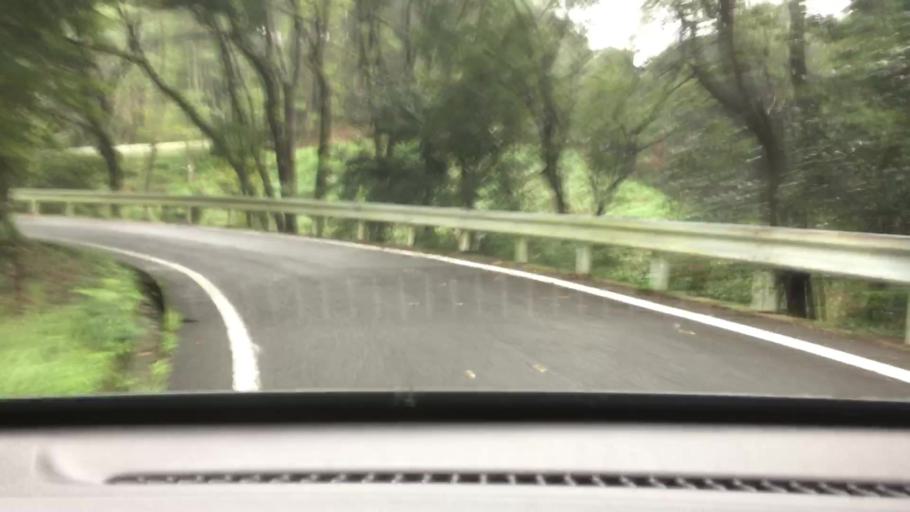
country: JP
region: Nagasaki
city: Togitsu
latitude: 32.9180
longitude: 129.7257
